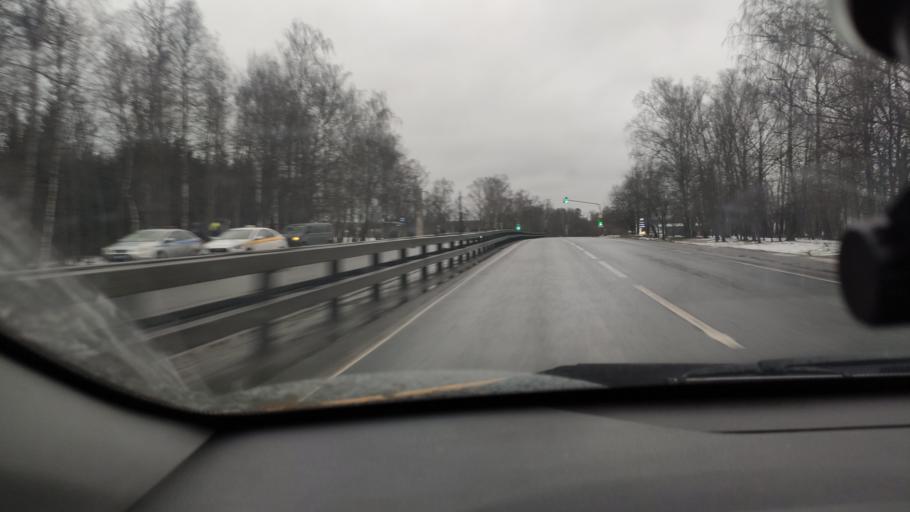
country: RU
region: Moskovskaya
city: Troitsk
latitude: 55.2995
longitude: 37.2015
